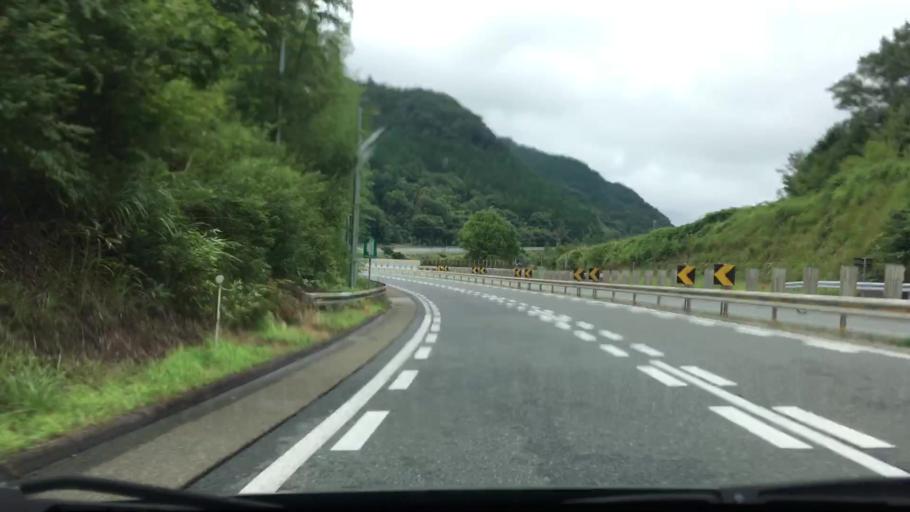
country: JP
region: Hiroshima
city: Shobara
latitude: 34.8511
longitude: 133.0931
